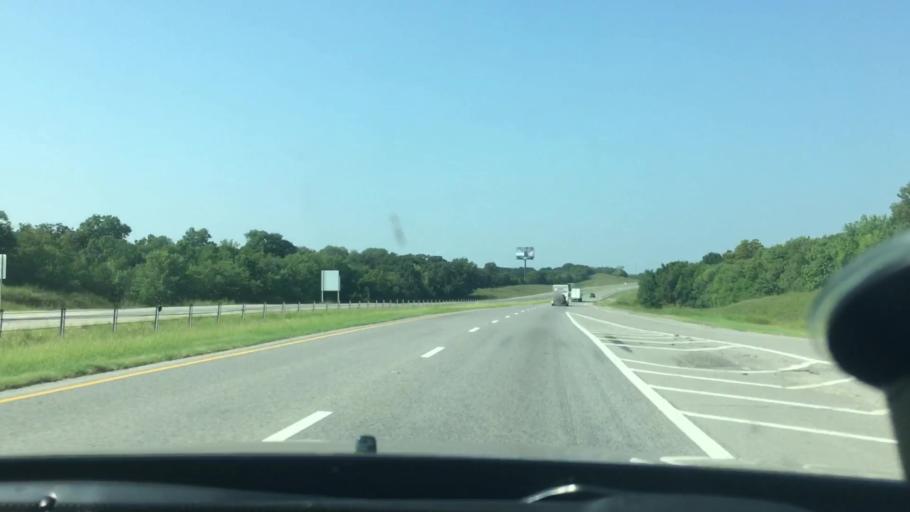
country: US
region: Oklahoma
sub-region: Bryan County
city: Durant
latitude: 34.0488
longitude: -96.3599
